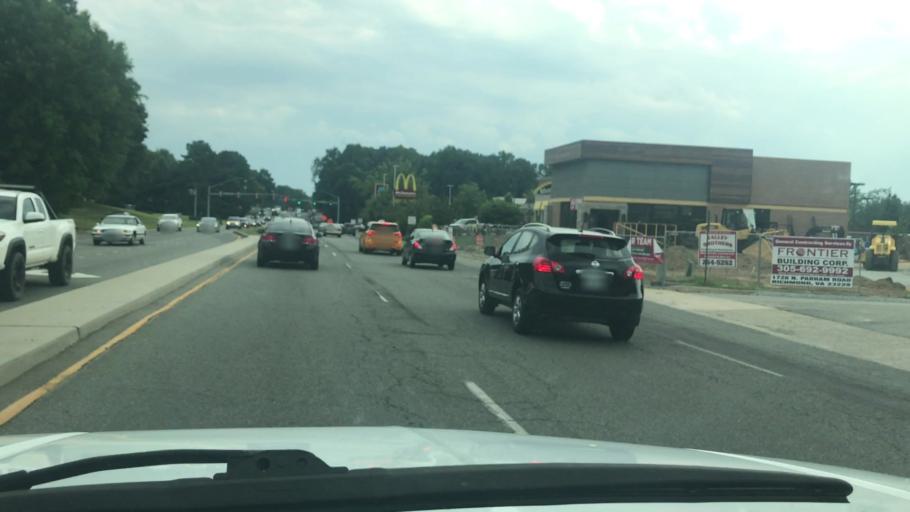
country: US
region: Virginia
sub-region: Henrico County
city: Tuckahoe
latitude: 37.6109
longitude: -77.5637
